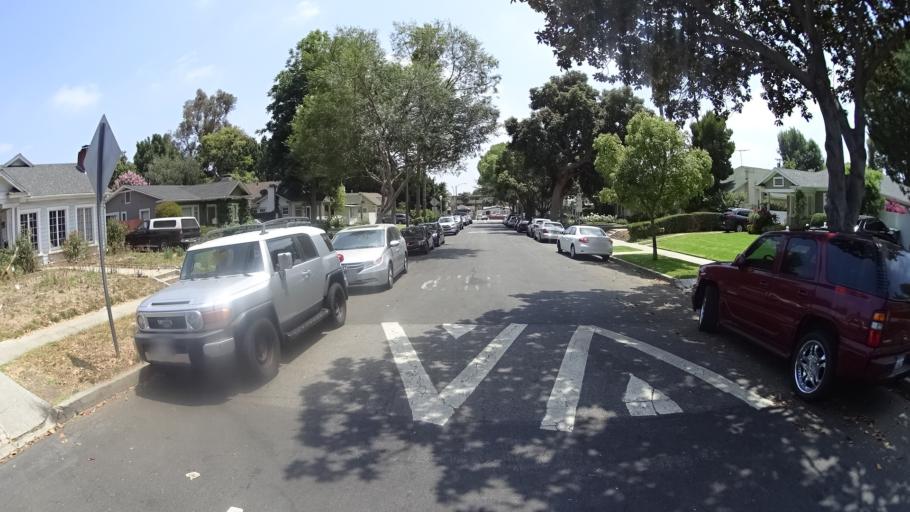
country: US
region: California
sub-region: Los Angeles County
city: West Hollywood
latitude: 34.0954
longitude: -118.3571
